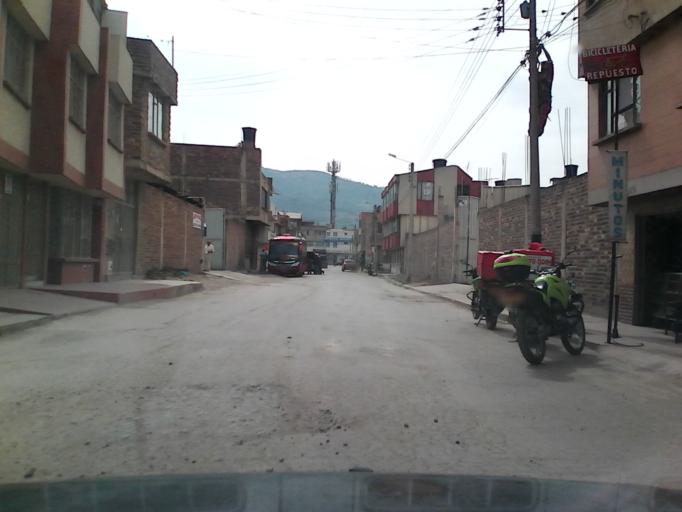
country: CO
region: Boyaca
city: Sogamoso
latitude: 5.7209
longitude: -72.9365
